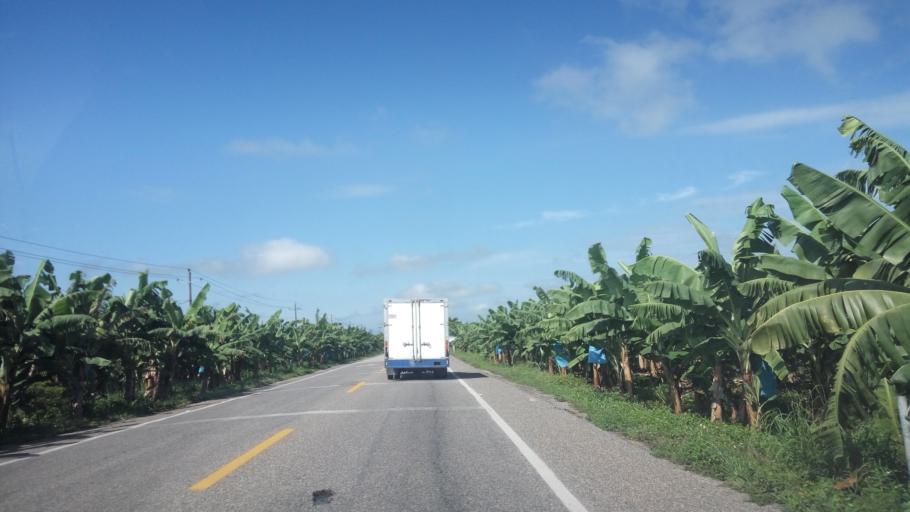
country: MX
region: Tabasco
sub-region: Teapa
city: Eureka y Belen
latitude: 17.6541
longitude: -92.9571
